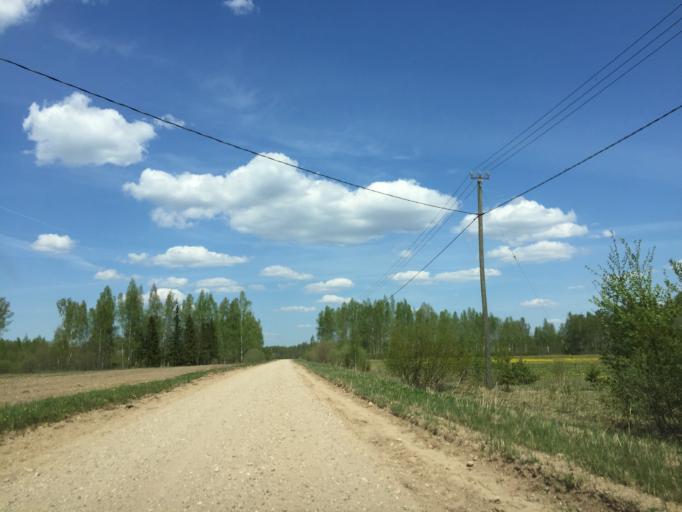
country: LV
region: Limbazu Rajons
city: Limbazi
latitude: 57.3908
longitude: 24.5725
